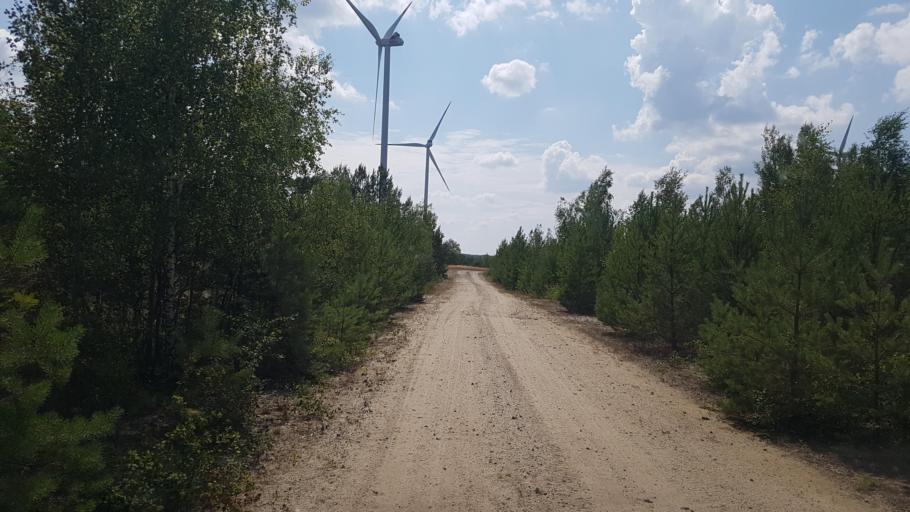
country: DE
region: Brandenburg
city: Sallgast
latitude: 51.5580
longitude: 13.8459
